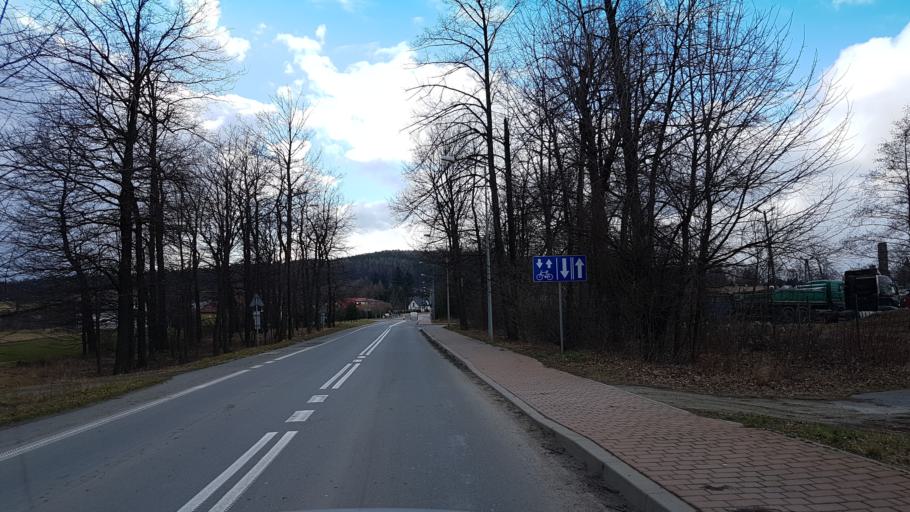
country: PL
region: Lesser Poland Voivodeship
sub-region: Powiat nowosadecki
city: Stary Sacz
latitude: 49.5542
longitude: 20.6439
